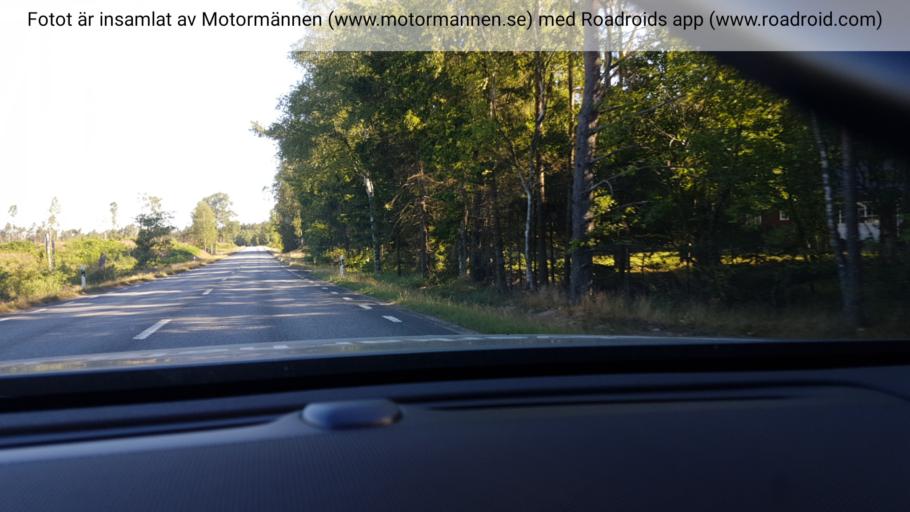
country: SE
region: Kronoberg
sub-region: Markaryds Kommun
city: Markaryd
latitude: 56.4217
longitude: 13.6265
